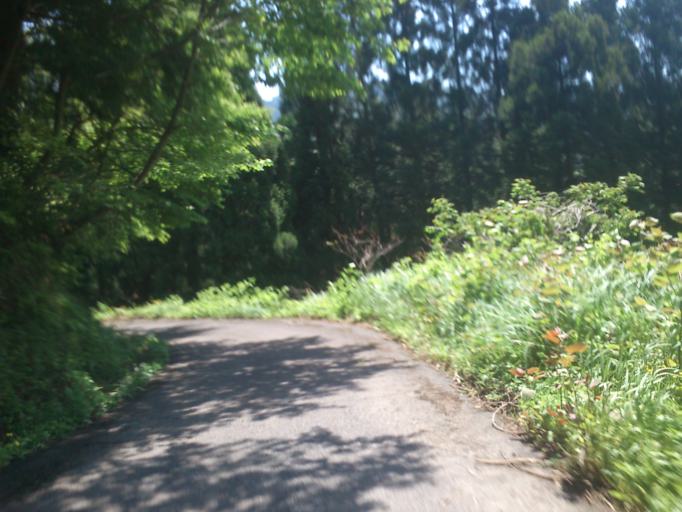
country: JP
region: Kyoto
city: Miyazu
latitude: 35.7126
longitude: 135.1562
